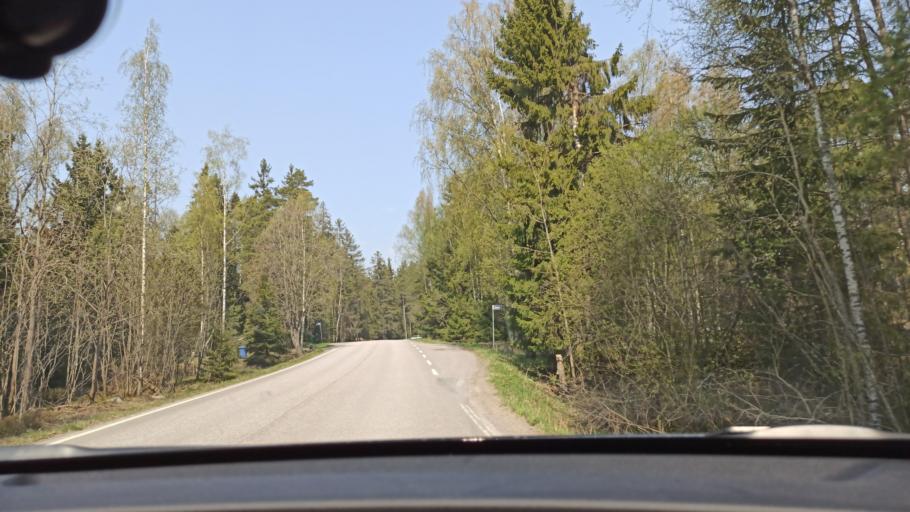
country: FI
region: Uusimaa
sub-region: Helsinki
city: Espoo
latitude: 60.0891
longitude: 24.5886
